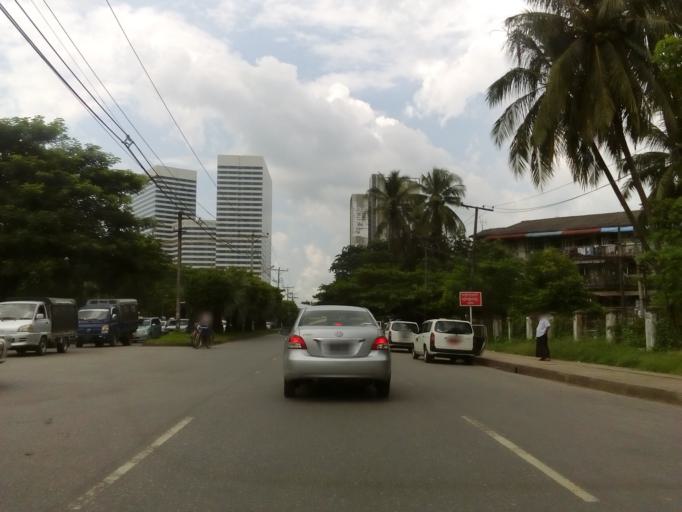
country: MM
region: Yangon
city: Yangon
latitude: 16.8255
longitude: 96.1594
